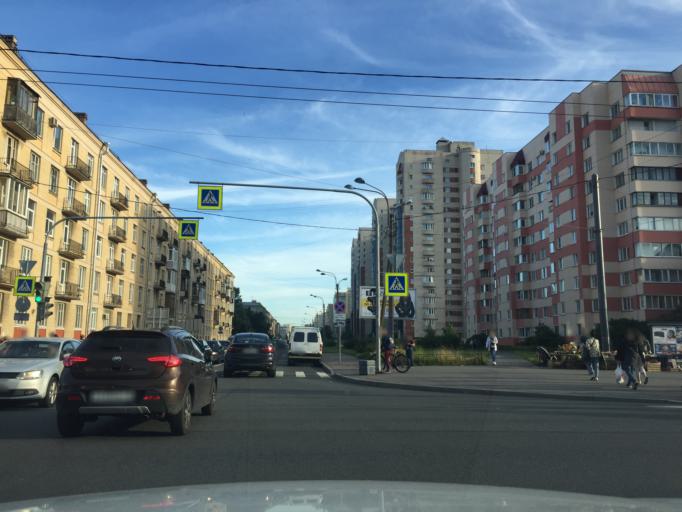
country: RU
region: St.-Petersburg
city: Admiralteisky
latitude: 59.8758
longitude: 30.3133
